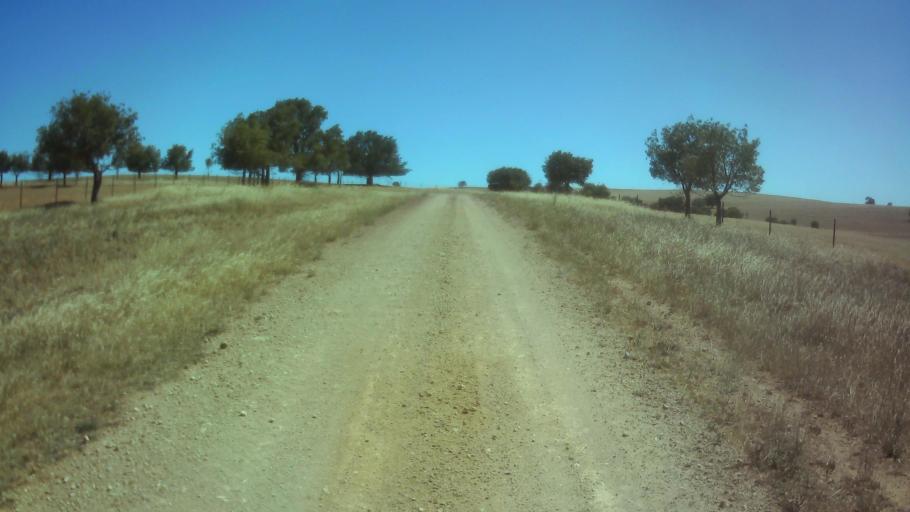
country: AU
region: New South Wales
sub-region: Weddin
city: Grenfell
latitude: -33.9681
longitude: 148.3615
